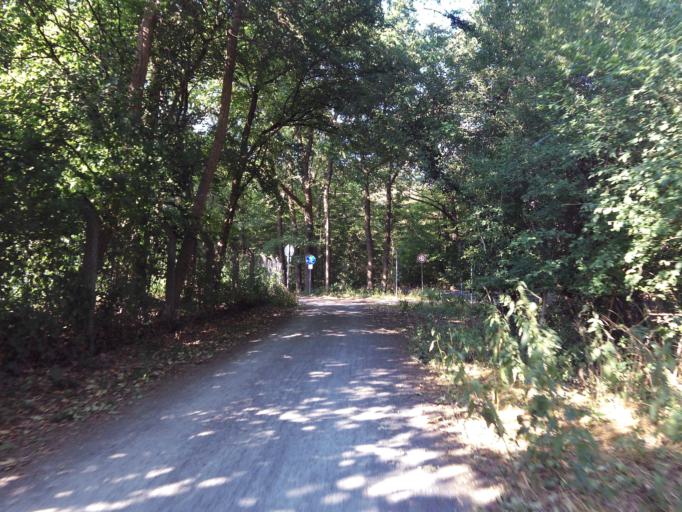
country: DE
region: Hesse
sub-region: Regierungsbezirk Darmstadt
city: Nauheim
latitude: 49.9706
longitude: 8.4569
